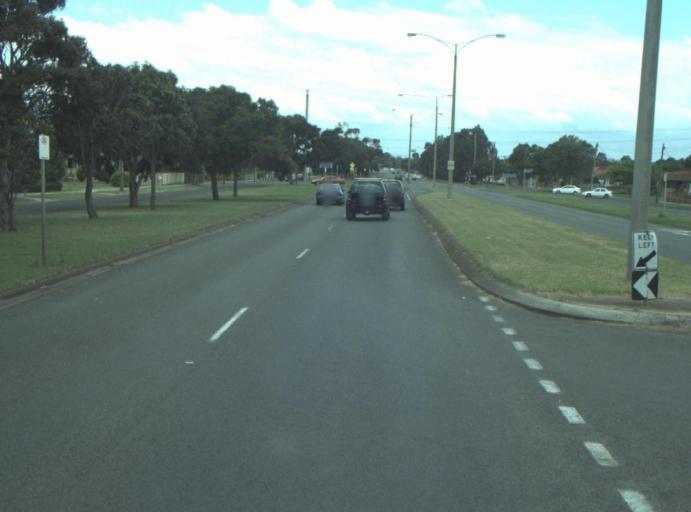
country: AU
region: Victoria
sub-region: Greater Geelong
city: Bell Park
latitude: -38.0770
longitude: 144.3586
